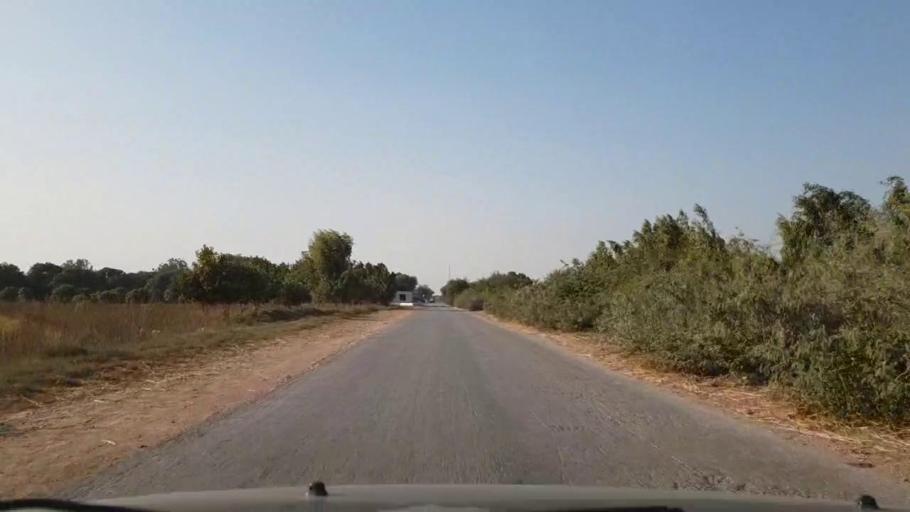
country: PK
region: Sindh
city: Chambar
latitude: 25.2063
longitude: 68.7872
